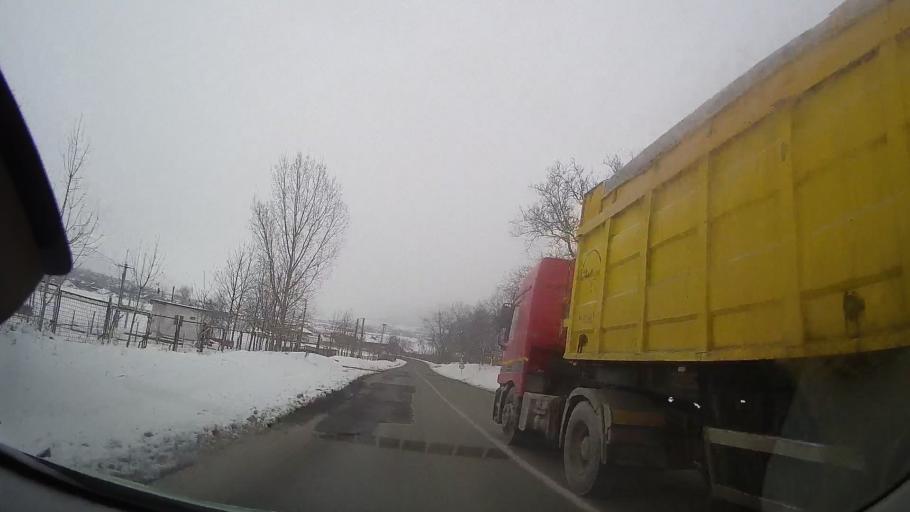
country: RO
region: Vaslui
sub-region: Comuna Todiresti
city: Todiresti
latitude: 46.8402
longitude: 27.3925
